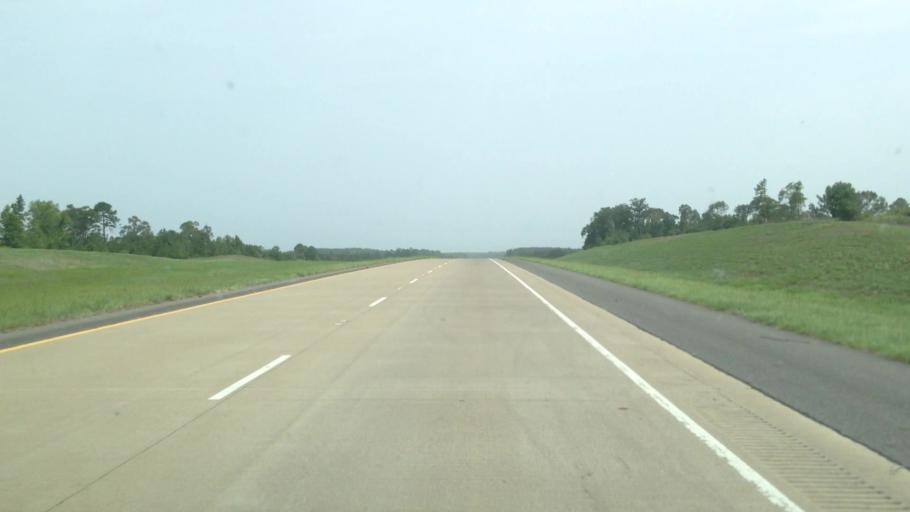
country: US
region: Louisiana
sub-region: Caddo Parish
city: Vivian
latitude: 32.9579
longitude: -93.9017
